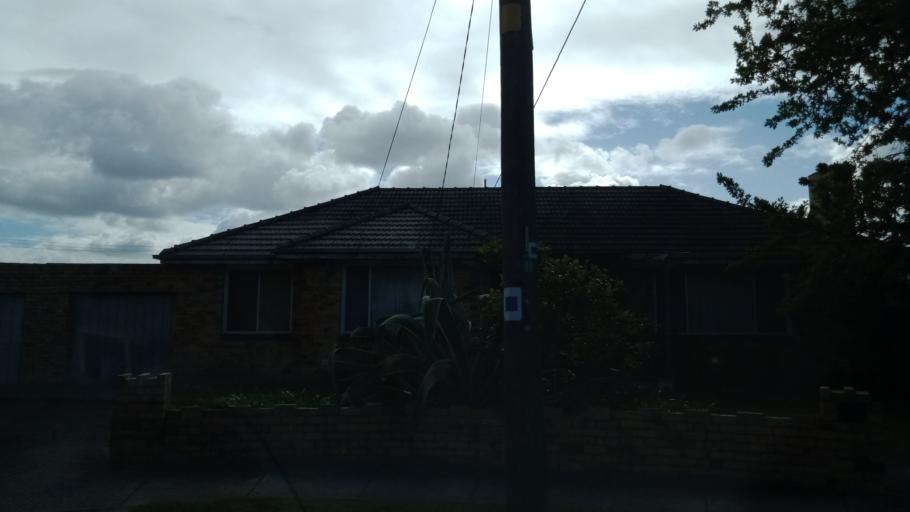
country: AU
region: Victoria
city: McKinnon
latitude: -37.9209
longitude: 145.0519
